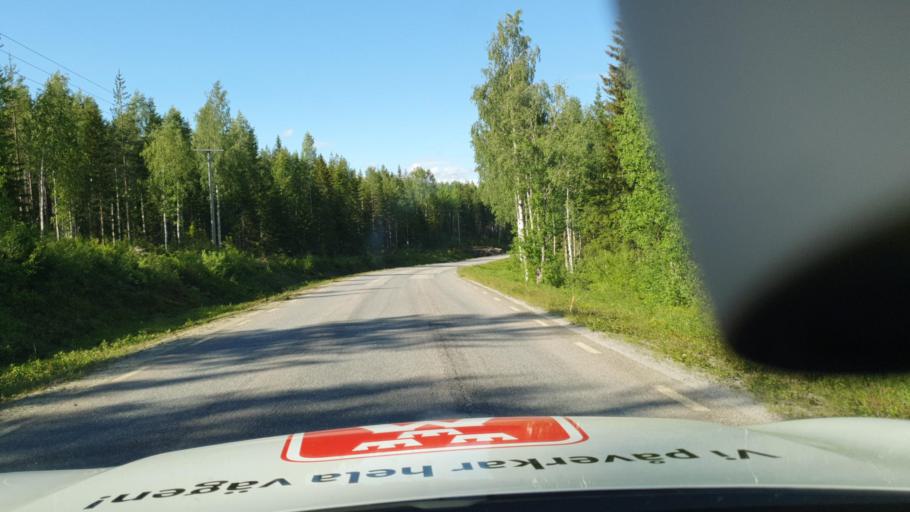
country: SE
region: Vaesterbotten
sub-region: Vannas Kommun
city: Vaennaes
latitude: 63.8789
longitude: 19.6834
